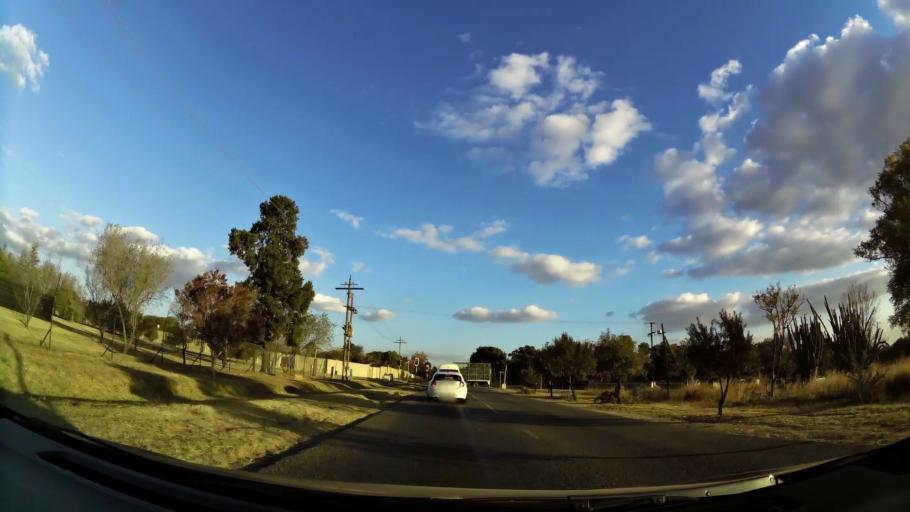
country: ZA
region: Gauteng
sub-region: City of Johannesburg Metropolitan Municipality
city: Midrand
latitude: -25.9663
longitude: 28.1536
